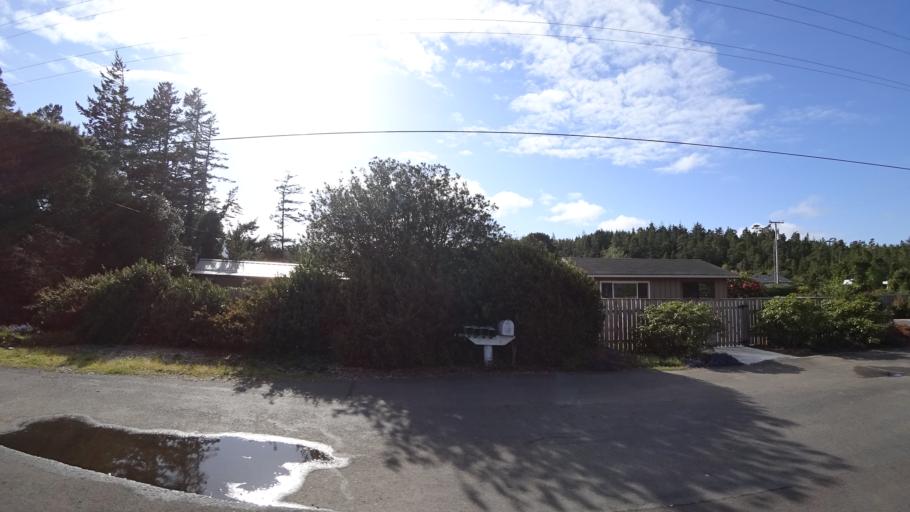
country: US
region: Oregon
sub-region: Lane County
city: Dunes City
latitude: 43.9031
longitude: -124.1154
